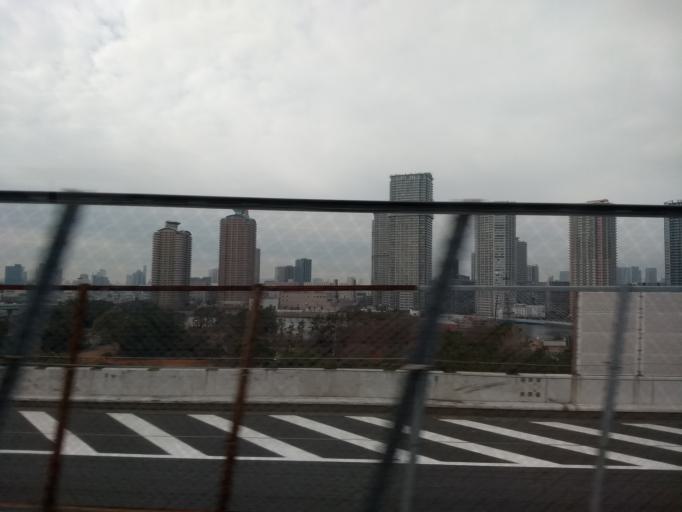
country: JP
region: Tokyo
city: Urayasu
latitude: 35.6458
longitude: 139.8124
